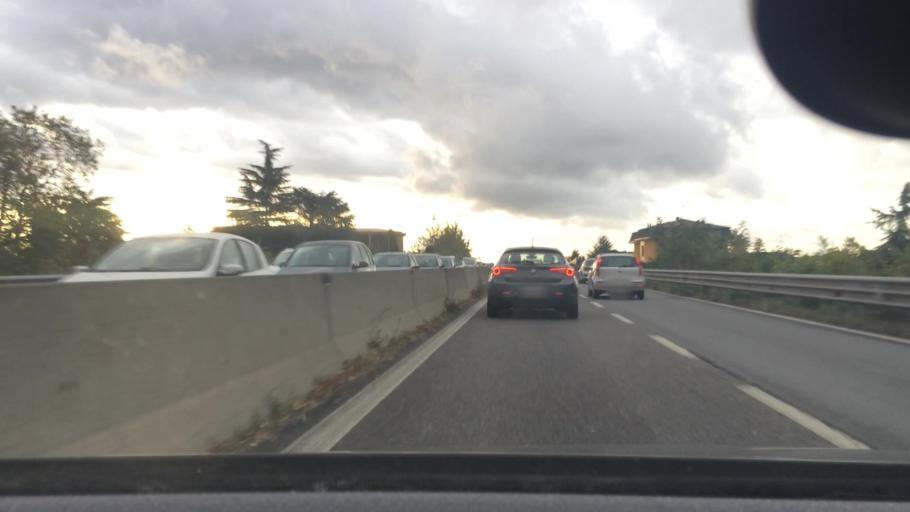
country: IT
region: Lombardy
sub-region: Citta metropolitana di Milano
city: Rho
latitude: 45.5363
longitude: 9.0484
